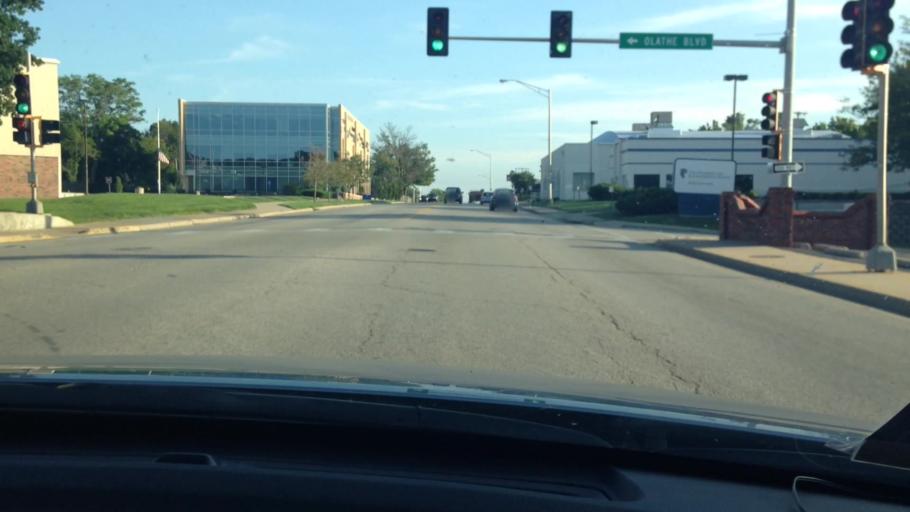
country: US
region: Kansas
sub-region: Johnson County
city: Westwood
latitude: 39.0539
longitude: -94.6119
